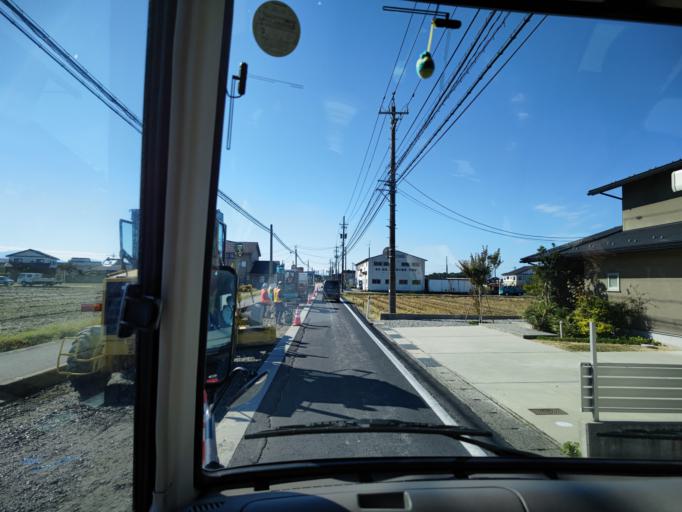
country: JP
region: Toyama
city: Nyuzen
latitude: 36.9009
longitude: 137.4221
